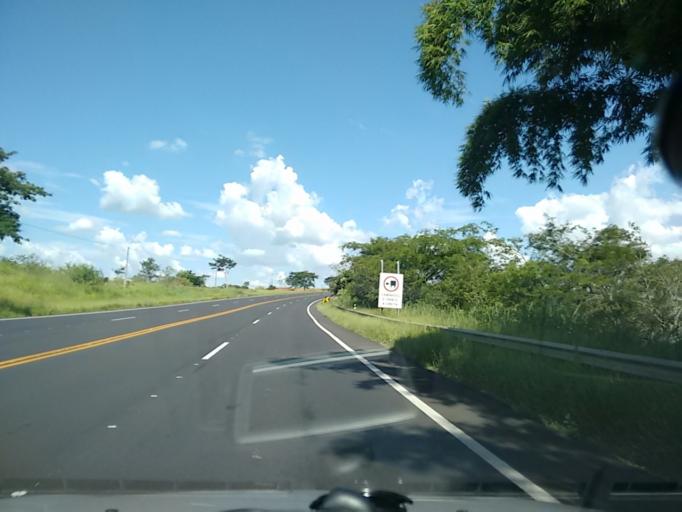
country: BR
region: Sao Paulo
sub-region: Pompeia
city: Pompeia
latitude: -22.1249
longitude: -50.1428
